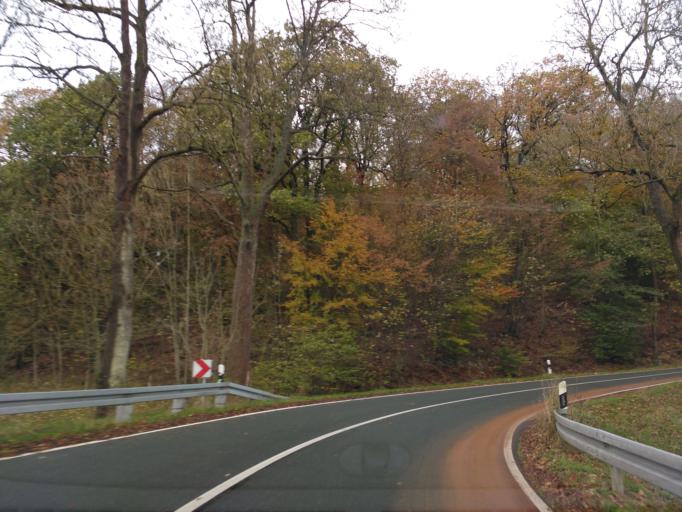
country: DE
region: Hesse
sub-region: Regierungsbezirk Kassel
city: Vohl
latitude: 51.1906
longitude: 8.9035
